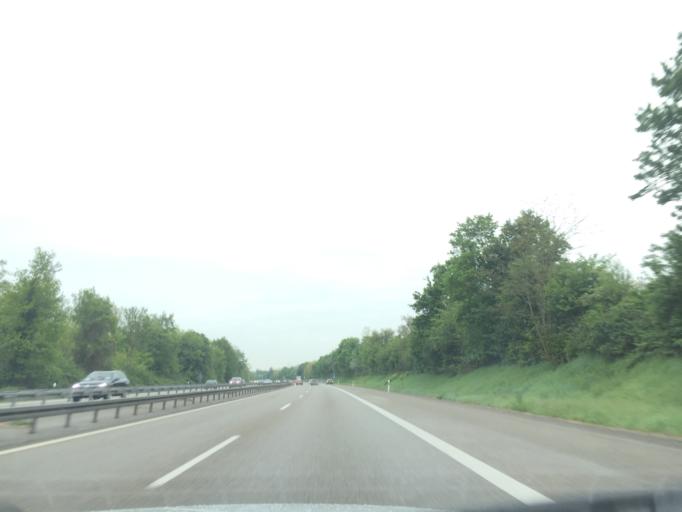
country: DE
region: Baden-Wuerttemberg
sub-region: Freiburg Region
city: Bad Bellingen
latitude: 47.7226
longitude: 7.5465
